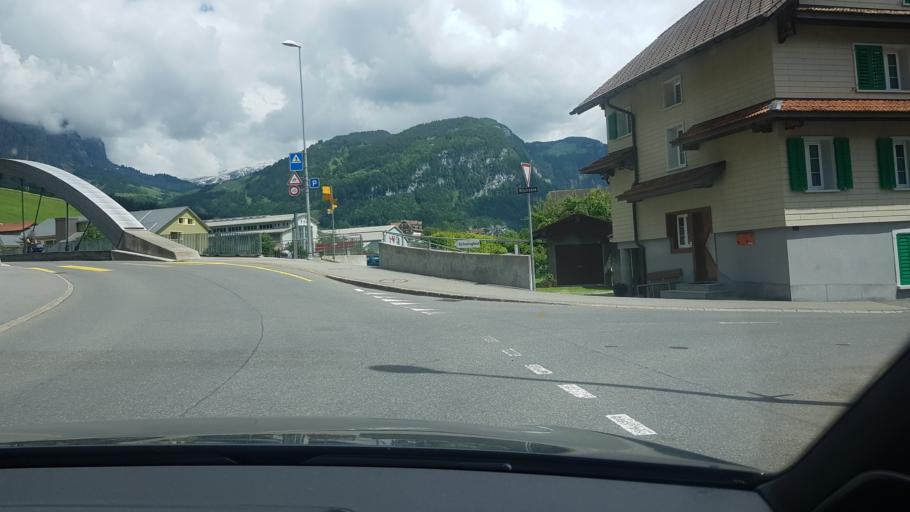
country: CH
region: Schwyz
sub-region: Bezirk Schwyz
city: Muotathal
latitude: 46.9761
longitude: 8.7563
